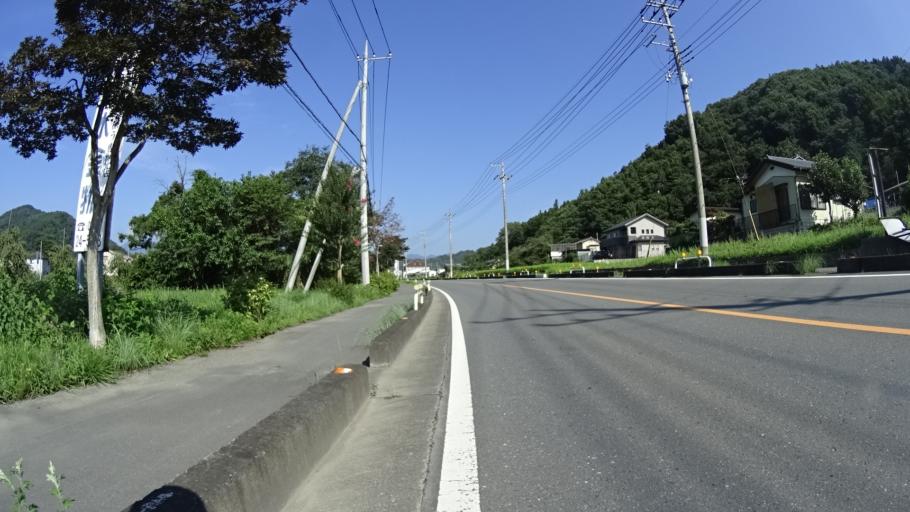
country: JP
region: Saitama
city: Chichibu
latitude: 36.0148
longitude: 139.0201
